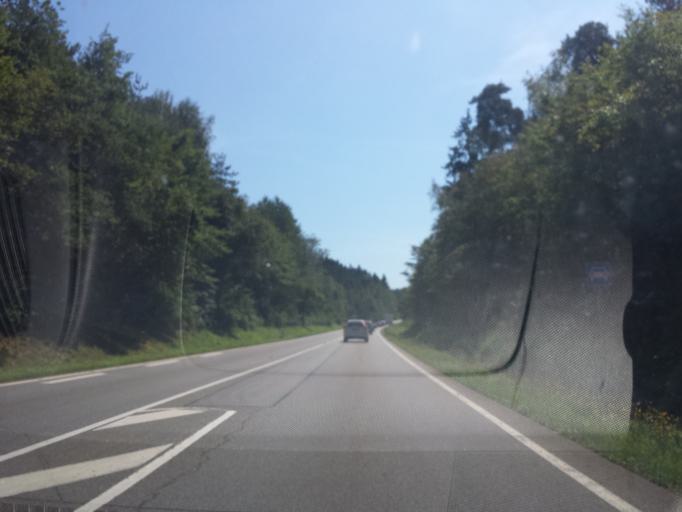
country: DE
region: Bavaria
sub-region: Lower Bavaria
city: Stallwang
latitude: 49.0599
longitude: 12.6433
